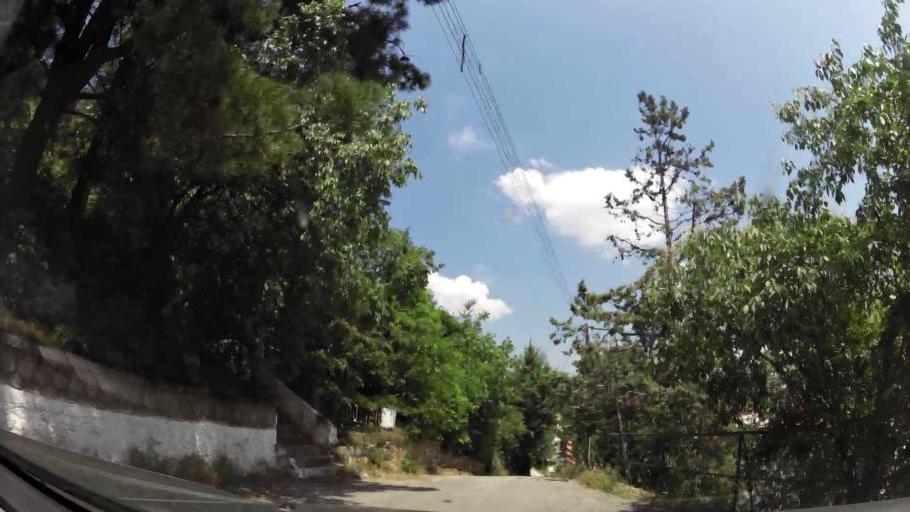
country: GR
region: West Macedonia
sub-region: Nomos Kozanis
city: Kozani
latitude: 40.3036
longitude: 21.7833
